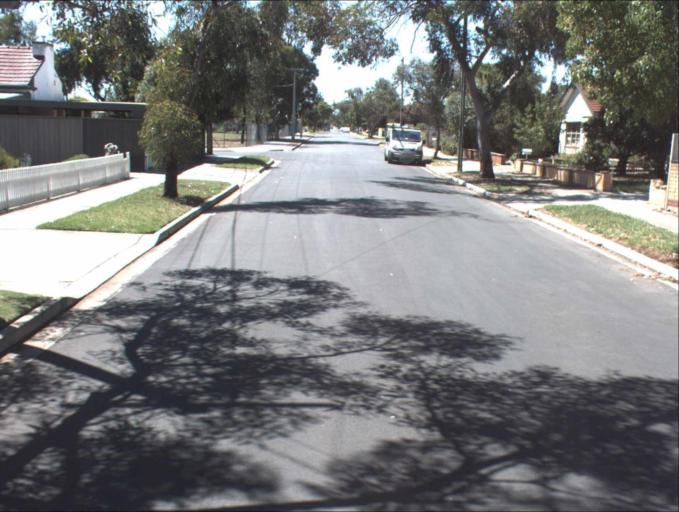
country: AU
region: South Australia
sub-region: Port Adelaide Enfield
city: Enfield
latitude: -34.8637
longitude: 138.6173
